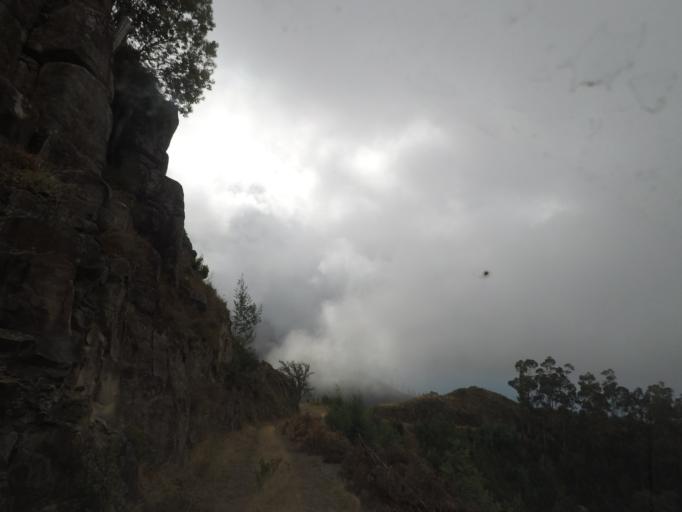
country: PT
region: Madeira
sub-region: Funchal
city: Nossa Senhora do Monte
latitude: 32.6949
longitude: -16.9120
